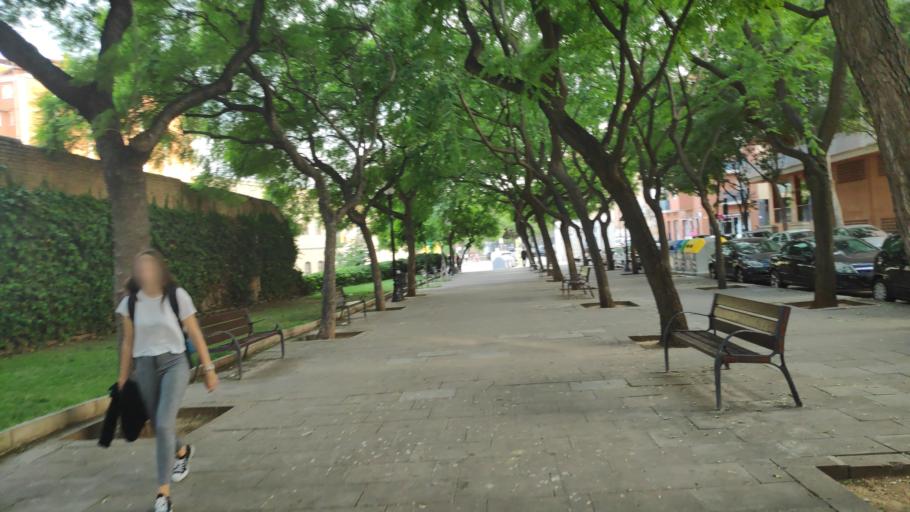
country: ES
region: Catalonia
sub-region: Provincia de Barcelona
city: Sant Marti
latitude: 41.4103
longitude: 2.1904
